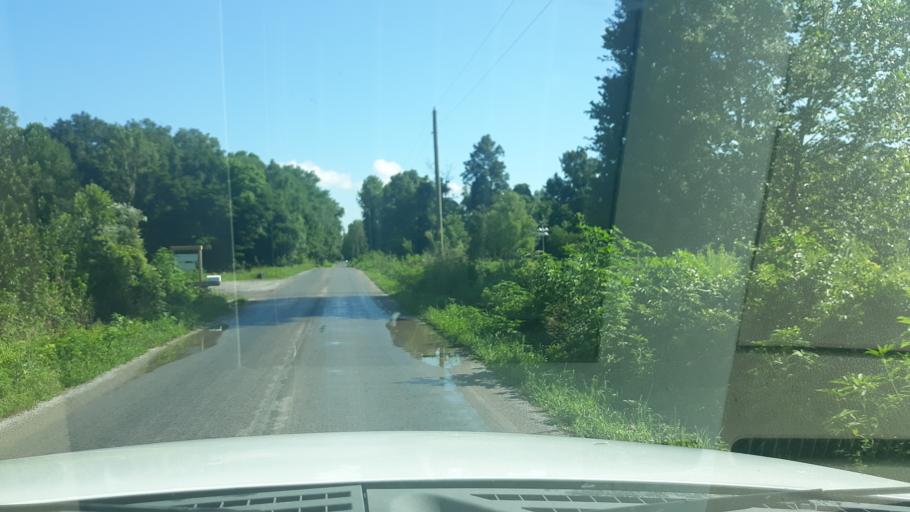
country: US
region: Illinois
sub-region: Saline County
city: Harrisburg
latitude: 37.8612
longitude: -88.5815
